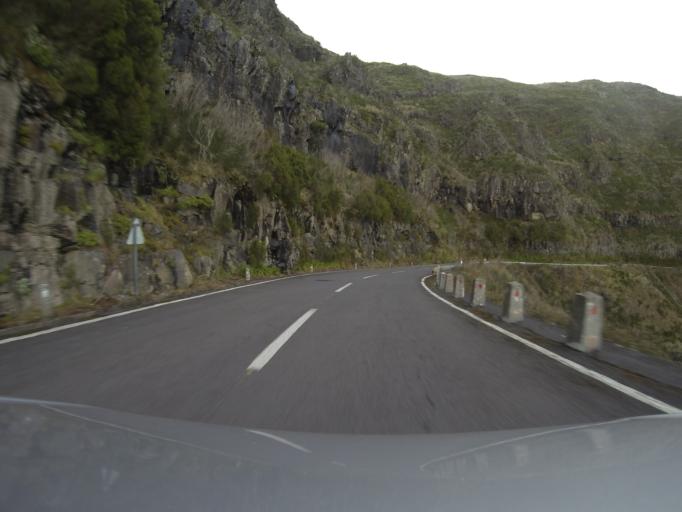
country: PT
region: Madeira
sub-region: Sao Vicente
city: Sao Vicente
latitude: 32.7389
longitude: -17.0504
